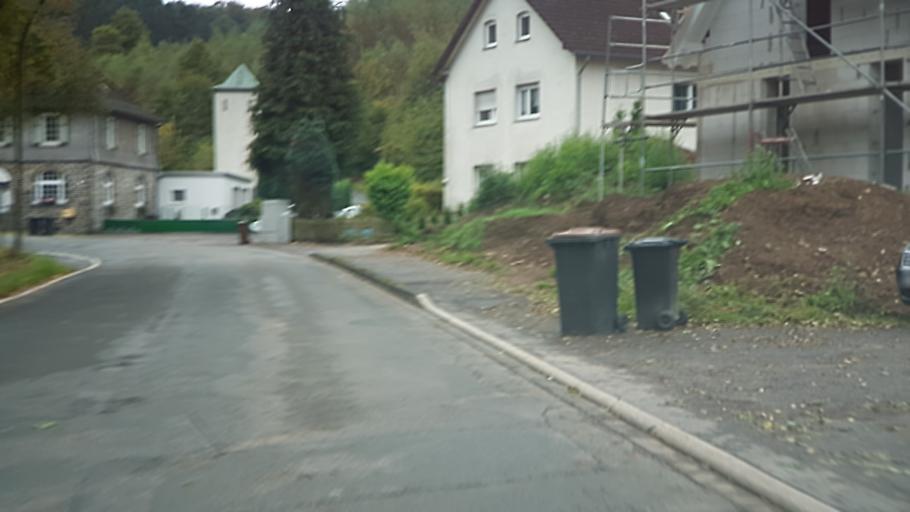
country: DE
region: North Rhine-Westphalia
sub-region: Regierungsbezirk Arnsberg
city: Herscheid
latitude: 51.2138
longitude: 7.6937
